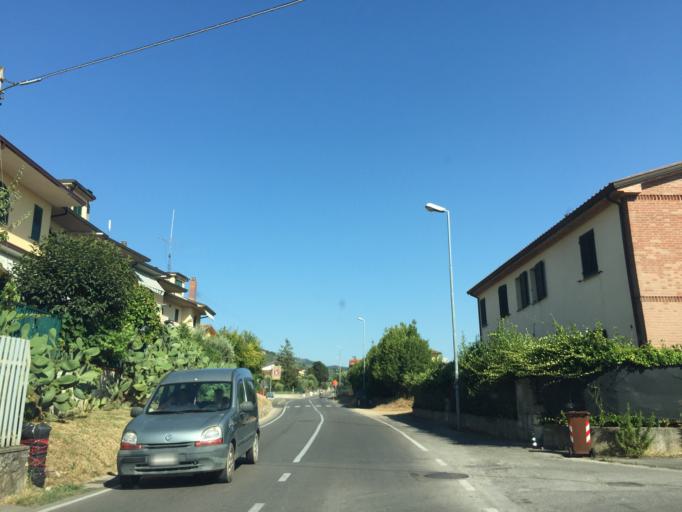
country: IT
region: Tuscany
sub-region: Provincia di Pistoia
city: Monsummano Terme
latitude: 43.8604
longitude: 10.8233
